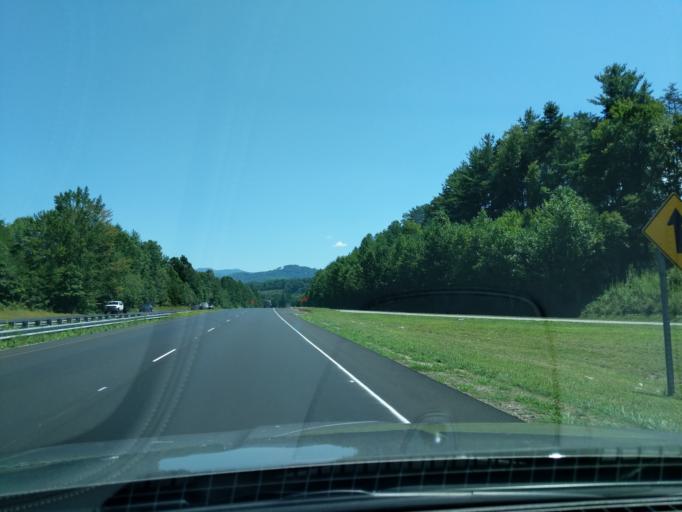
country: US
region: North Carolina
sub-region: Macon County
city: Franklin
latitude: 35.1657
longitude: -83.3866
